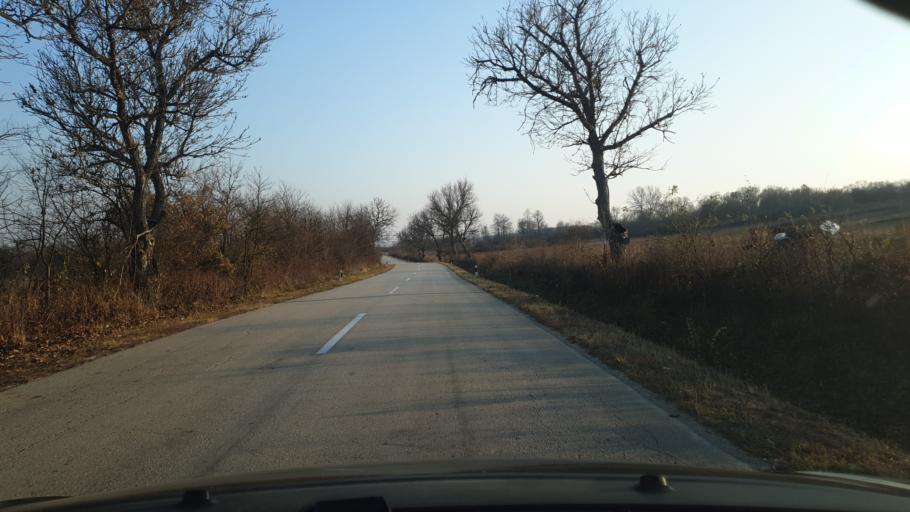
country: RS
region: Central Serbia
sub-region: Zajecarski Okrug
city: Zajecar
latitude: 43.9842
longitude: 22.2873
